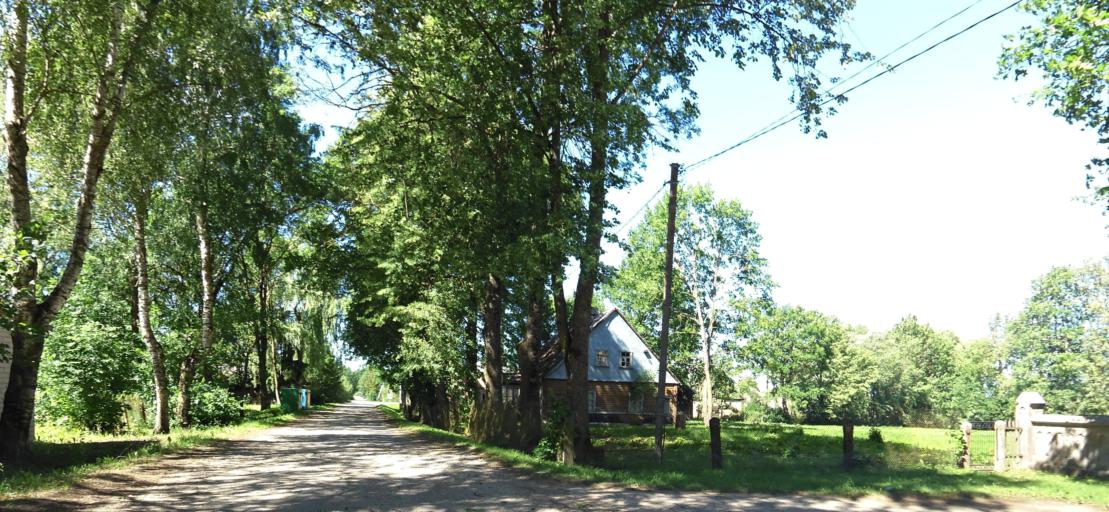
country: LV
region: Bauskas Rajons
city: Bauska
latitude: 56.2344
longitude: 24.2317
